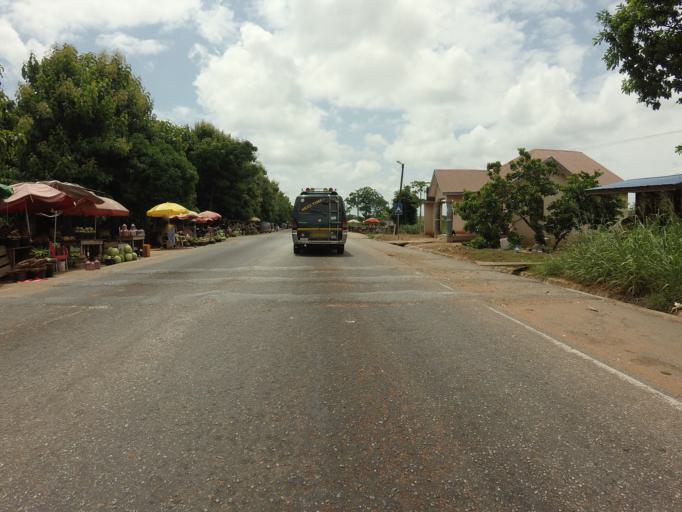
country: GH
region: Brong-Ahafo
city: Techiman
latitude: 7.6518
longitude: -1.8772
